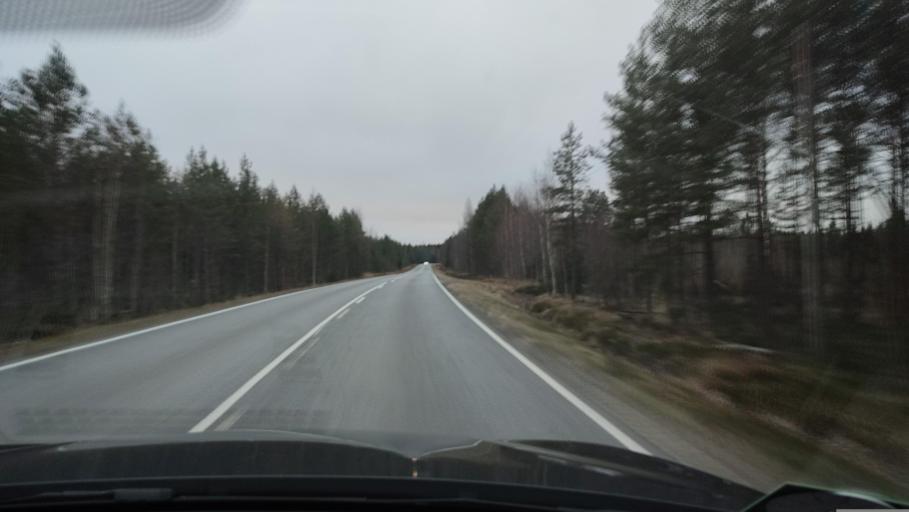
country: FI
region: Southern Ostrobothnia
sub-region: Suupohja
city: Karijoki
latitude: 62.3271
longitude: 21.8959
